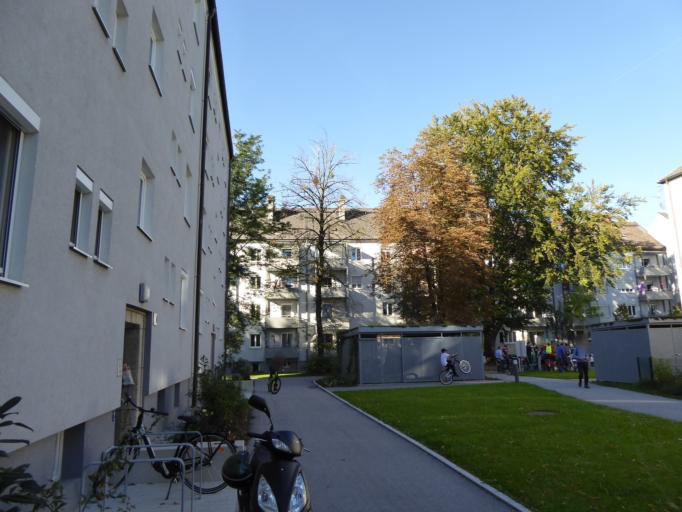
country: AT
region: Salzburg
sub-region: Salzburg Stadt
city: Salzburg
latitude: 47.8097
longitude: 13.0286
